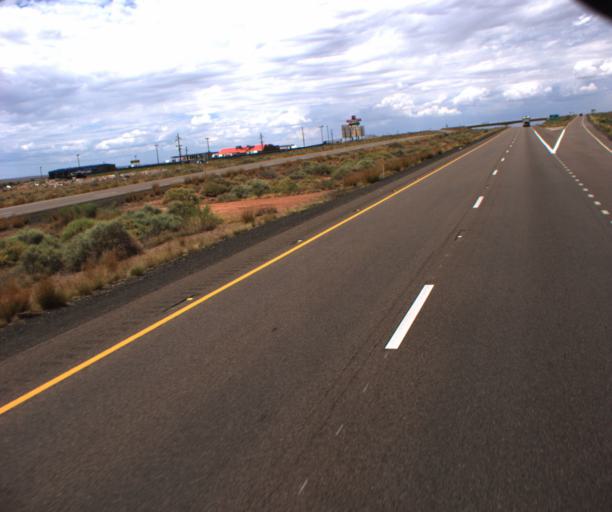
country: US
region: Arizona
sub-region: Navajo County
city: Holbrook
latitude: 34.9067
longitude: -110.2056
